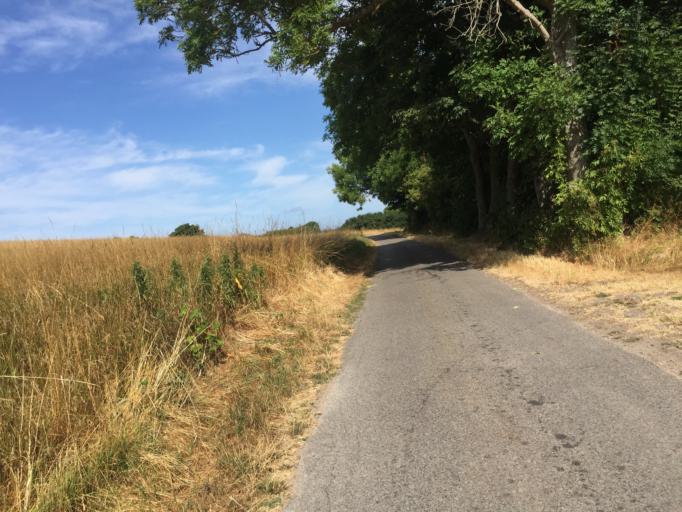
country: DK
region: Central Jutland
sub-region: Samso Kommune
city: Tranebjerg
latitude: 55.9512
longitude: 10.4302
